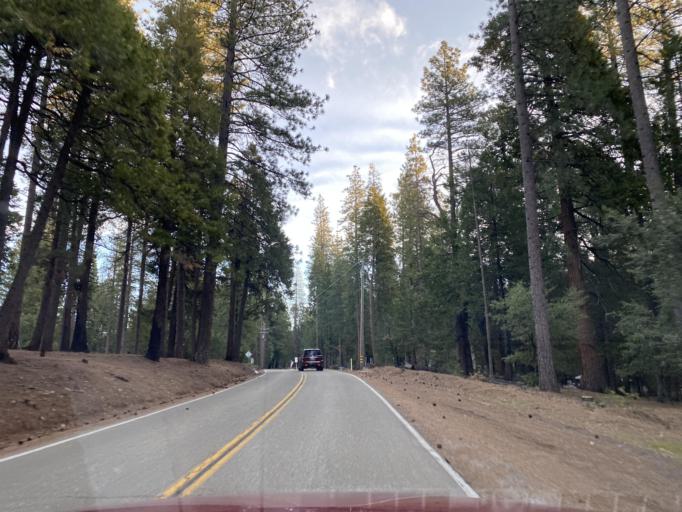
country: US
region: California
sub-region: Amador County
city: Pioneer
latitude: 38.4993
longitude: -120.5573
